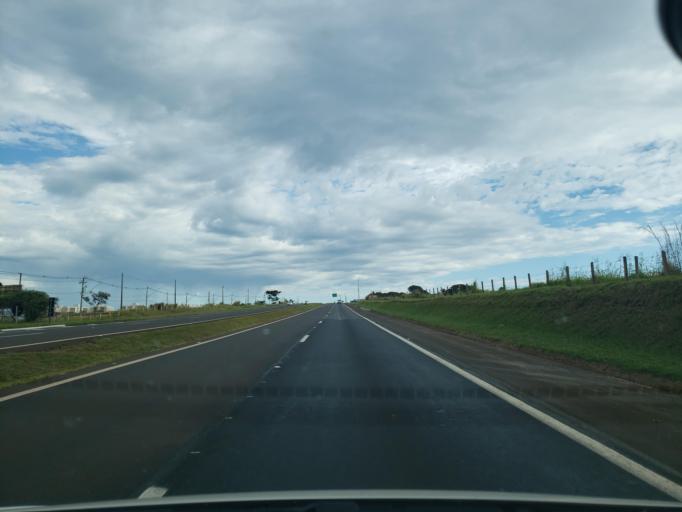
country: BR
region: Sao Paulo
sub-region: Jau
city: Jau
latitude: -22.2591
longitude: -48.5423
